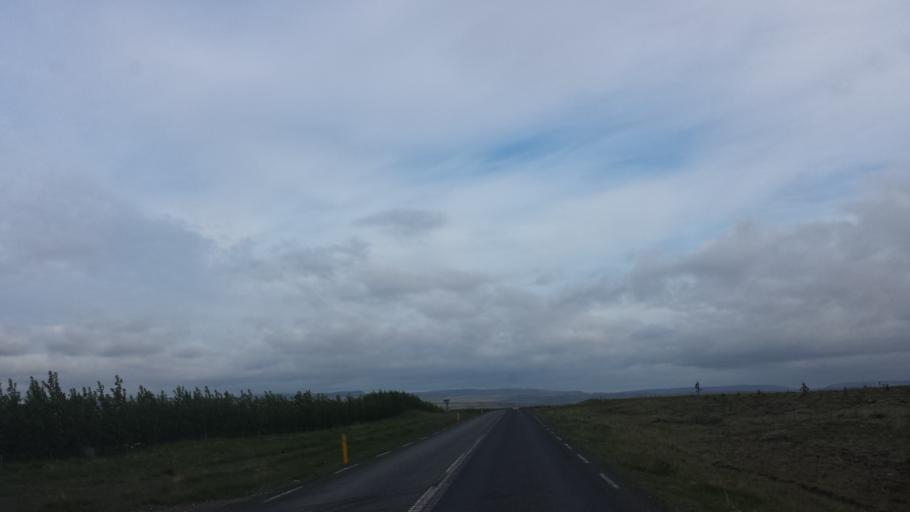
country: IS
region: South
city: Selfoss
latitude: 64.2714
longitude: -20.3550
